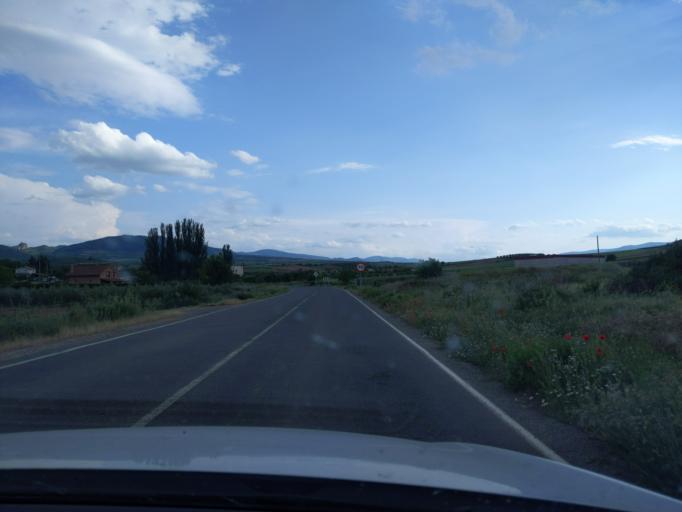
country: ES
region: La Rioja
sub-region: Provincia de La Rioja
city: Alberite
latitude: 42.3998
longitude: -2.4267
